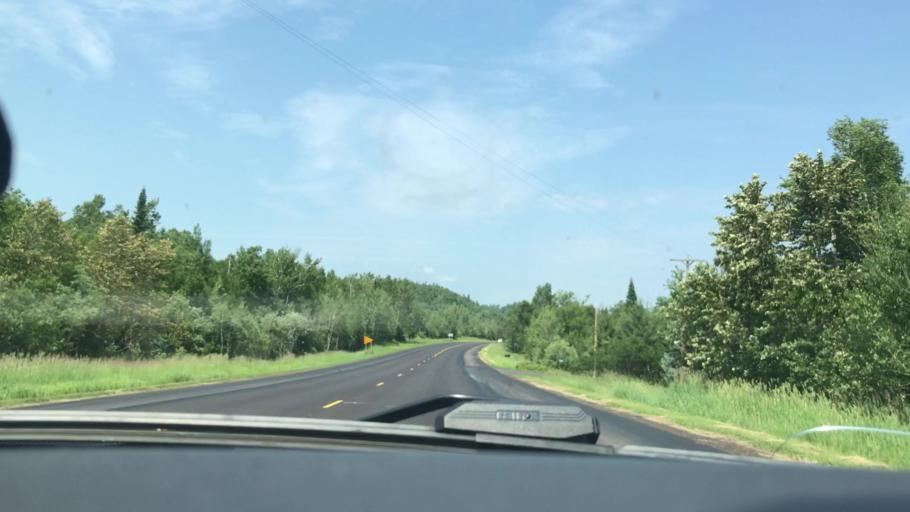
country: US
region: Minnesota
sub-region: Lake County
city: Silver Bay
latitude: 47.3530
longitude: -91.1823
